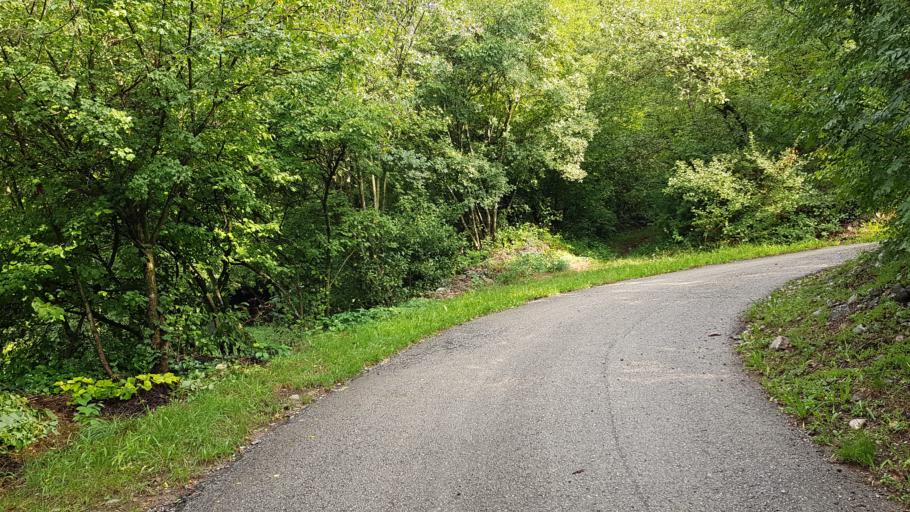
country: IT
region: Trentino-Alto Adige
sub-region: Provincia di Trento
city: Vezzano
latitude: 46.0849
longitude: 10.9984
